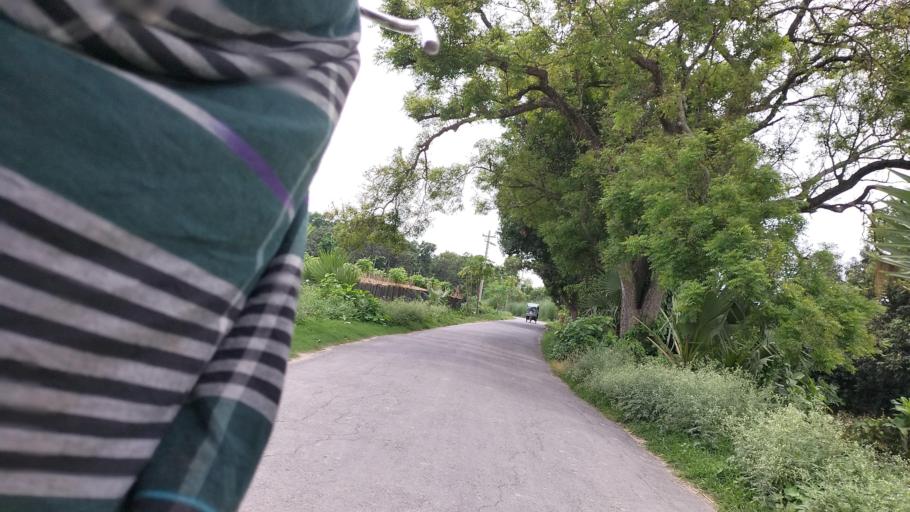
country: BD
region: Rajshahi
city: Rajshahi
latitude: 24.5143
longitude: 88.6314
